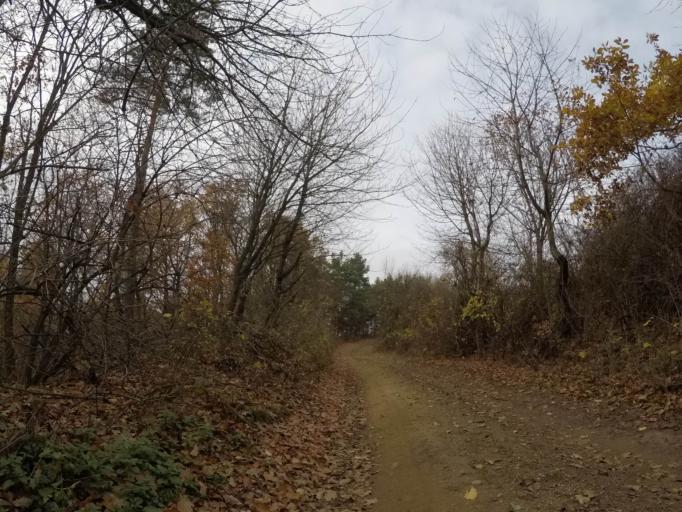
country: SK
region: Presovsky
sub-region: Okres Presov
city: Presov
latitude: 48.9249
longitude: 21.1432
